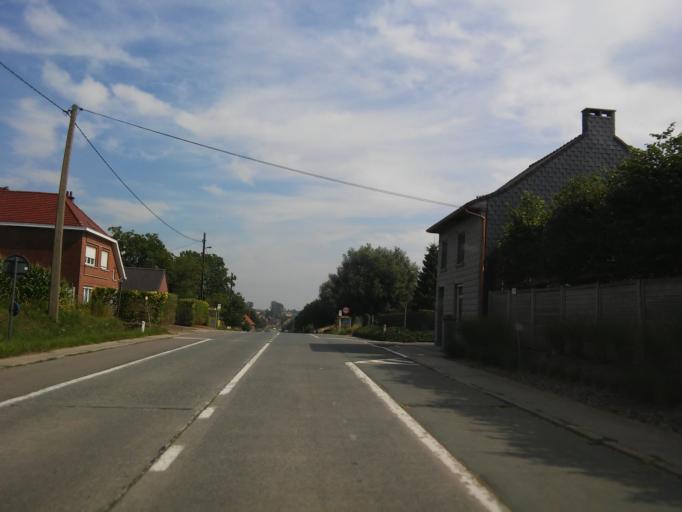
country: BE
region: Flanders
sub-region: Provincie Vlaams-Brabant
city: Gooik
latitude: 50.7535
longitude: 4.1042
